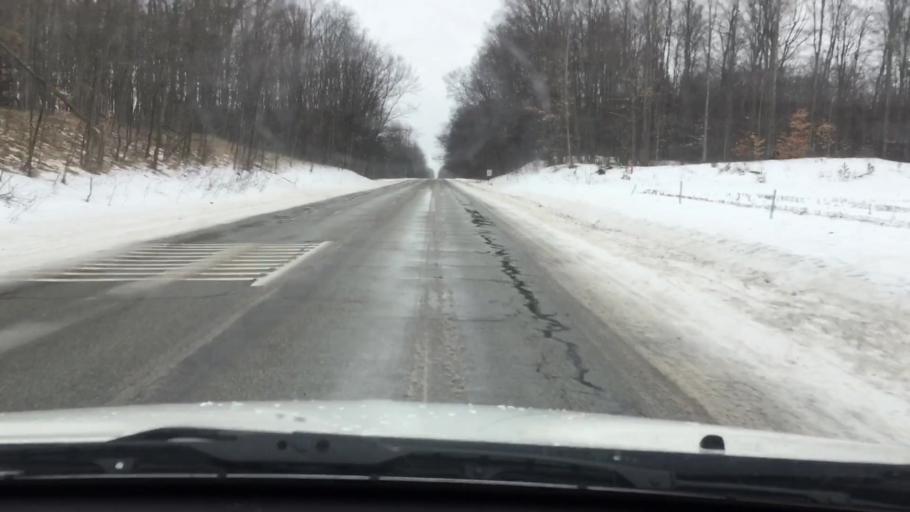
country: US
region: Michigan
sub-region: Wexford County
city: Cadillac
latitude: 44.1982
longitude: -85.4057
